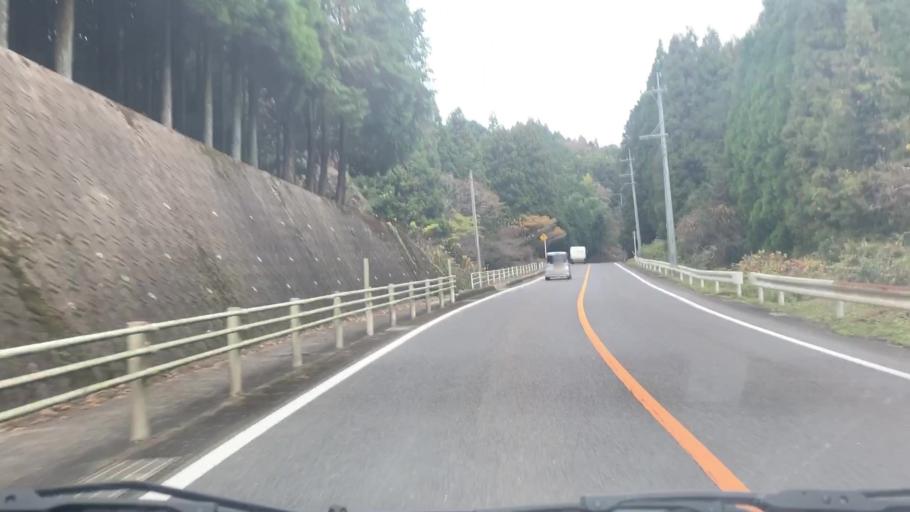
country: JP
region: Saga Prefecture
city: Ureshinomachi-shimojuku
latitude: 33.1606
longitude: 129.9681
